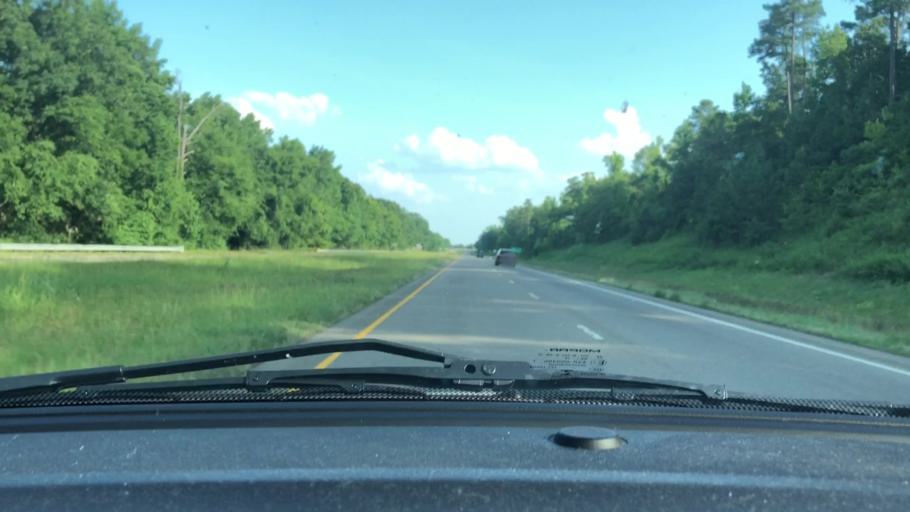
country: US
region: North Carolina
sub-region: Chatham County
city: Farmville
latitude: 35.5921
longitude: -79.3158
